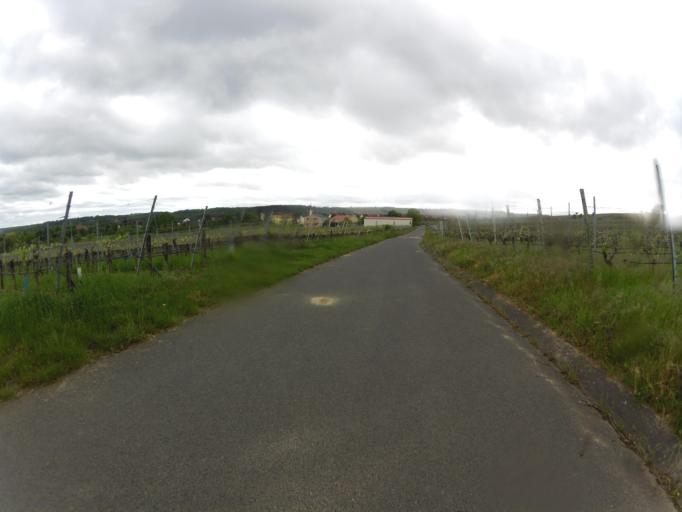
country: DE
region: Bavaria
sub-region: Regierungsbezirk Unterfranken
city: Sommerach
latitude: 49.8342
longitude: 10.2153
